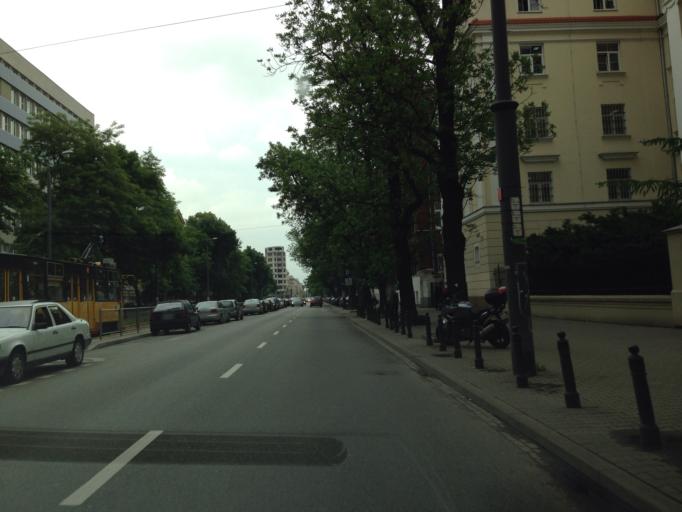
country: PL
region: Masovian Voivodeship
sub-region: Warszawa
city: Warsaw
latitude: 52.2201
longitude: 21.0070
